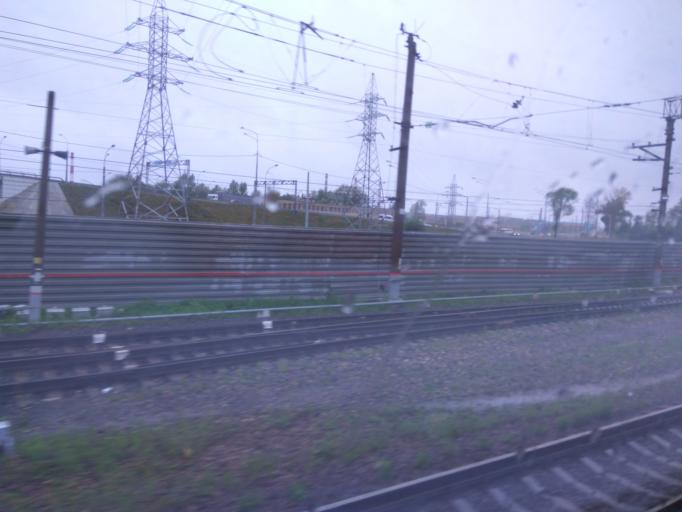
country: RU
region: Moskovskaya
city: Stupino
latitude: 54.9056
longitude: 38.0820
